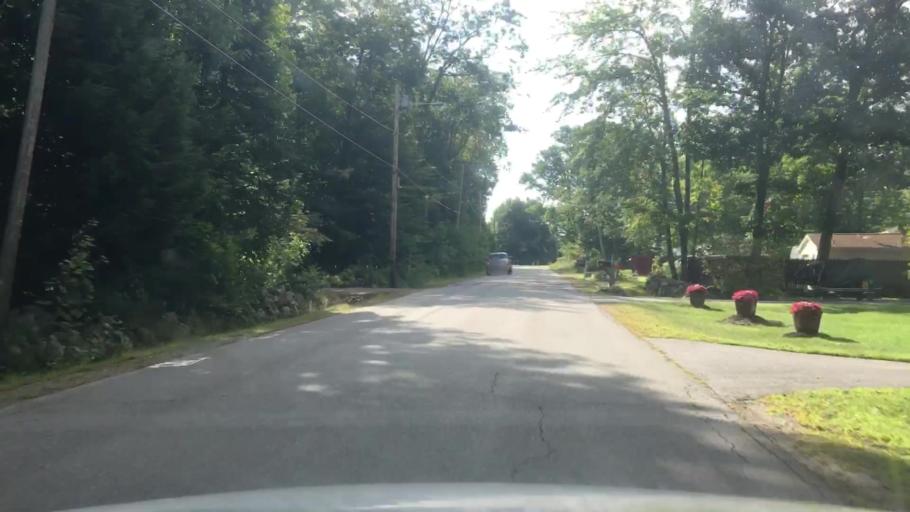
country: US
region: Maine
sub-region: Kennebec County
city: Gardiner
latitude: 44.1720
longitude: -69.8177
